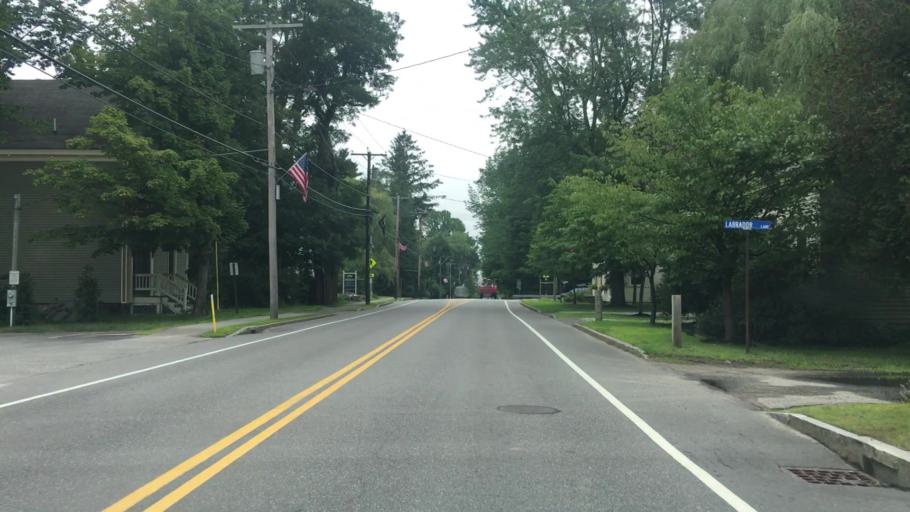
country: US
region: Maine
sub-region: Sagadahoc County
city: Topsham
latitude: 43.9294
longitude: -69.9643
